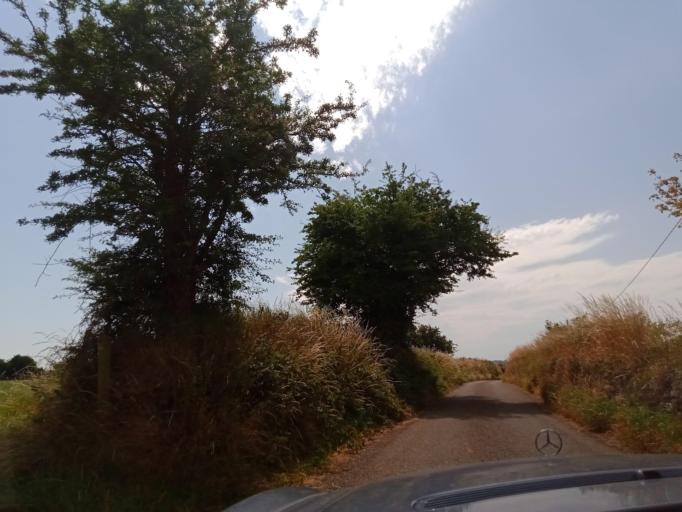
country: IE
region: Leinster
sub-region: Kilkenny
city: Mooncoin
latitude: 52.2672
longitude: -7.2282
